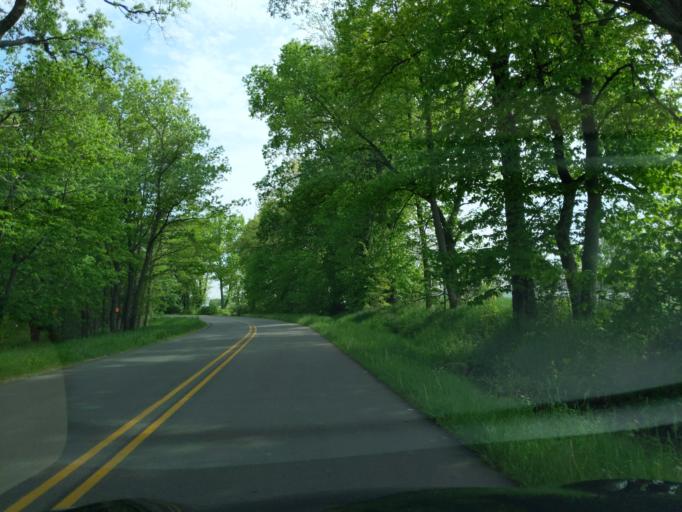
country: US
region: Michigan
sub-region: Ingham County
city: Leslie
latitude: 42.4199
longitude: -84.3567
